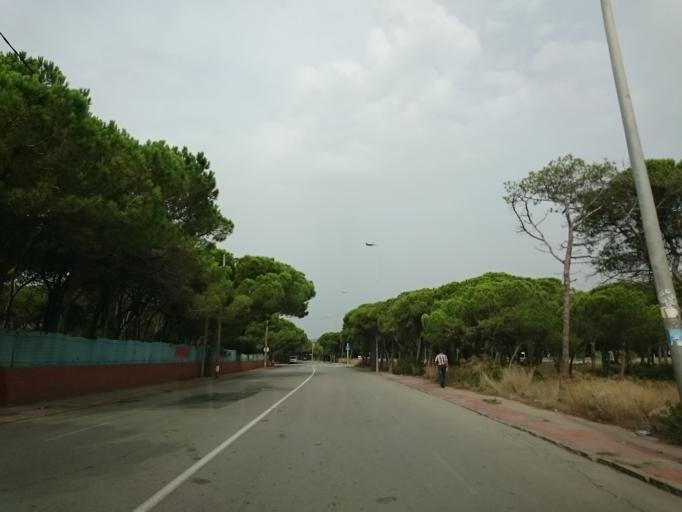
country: ES
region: Catalonia
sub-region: Provincia de Barcelona
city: Viladecans
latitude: 41.2708
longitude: 2.0363
